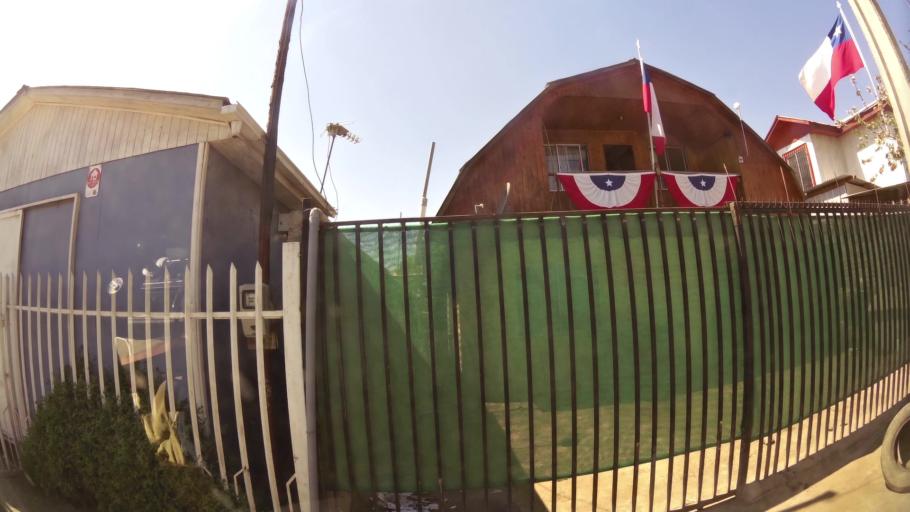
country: CL
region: Santiago Metropolitan
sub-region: Provincia de Talagante
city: Penaflor
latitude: -33.5828
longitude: -70.8089
